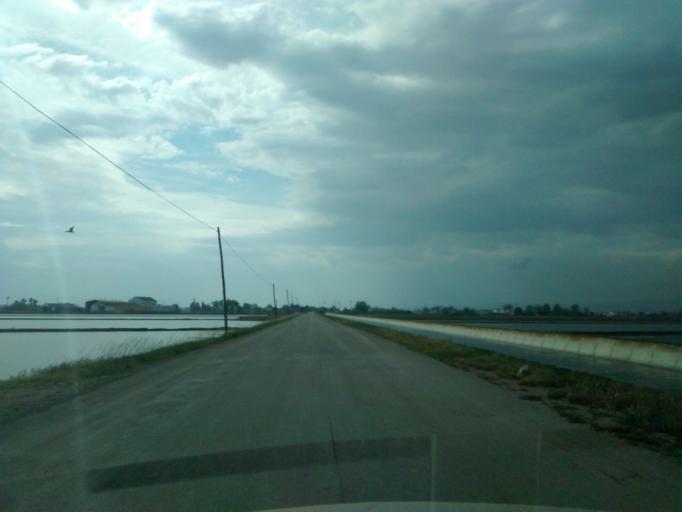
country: ES
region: Catalonia
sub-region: Provincia de Tarragona
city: Deltebre
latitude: 40.7001
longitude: 0.7477
